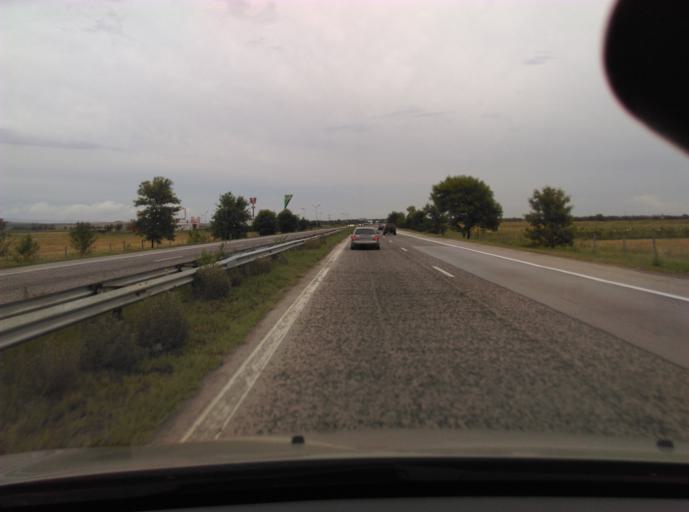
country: BG
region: Plovdiv
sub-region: Obshtina Rakovski
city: Rakovski
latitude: 42.2186
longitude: 25.0379
